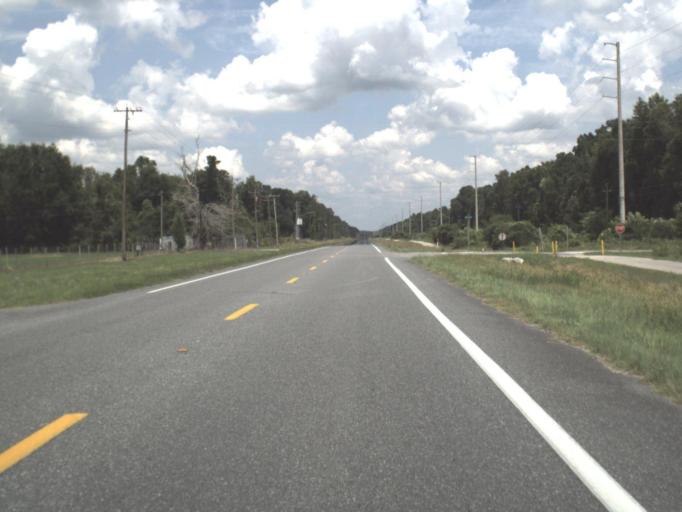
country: US
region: Florida
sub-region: Alachua County
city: High Springs
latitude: 29.9525
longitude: -82.8271
